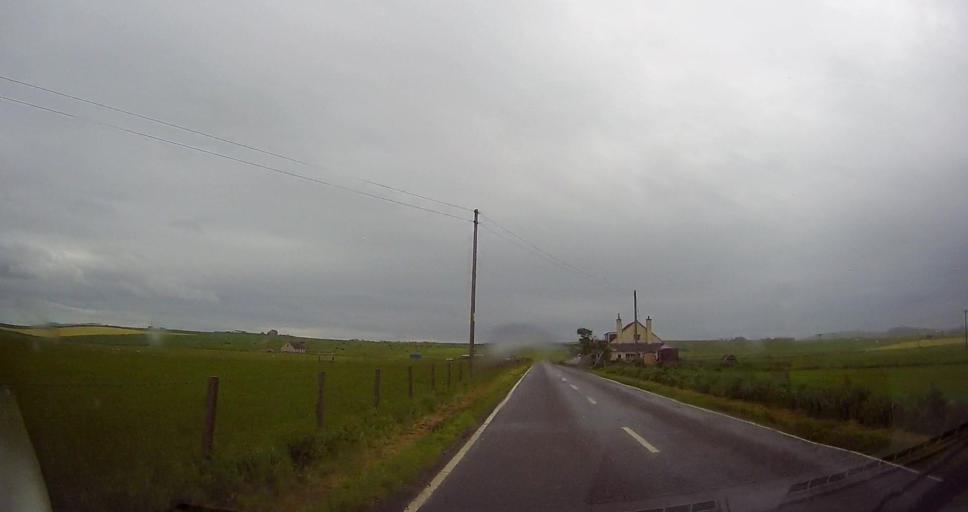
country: GB
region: Scotland
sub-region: Orkney Islands
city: Stromness
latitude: 59.0396
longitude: -3.2824
